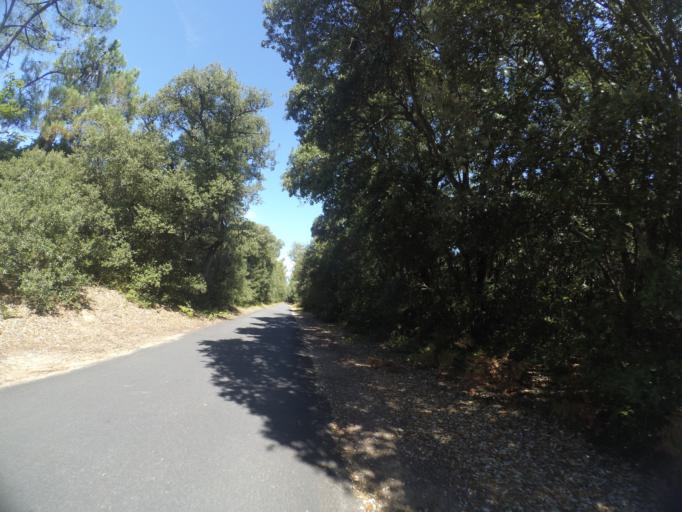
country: FR
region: Poitou-Charentes
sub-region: Departement de la Charente-Maritime
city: Les Mathes
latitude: 45.6736
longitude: -1.1498
